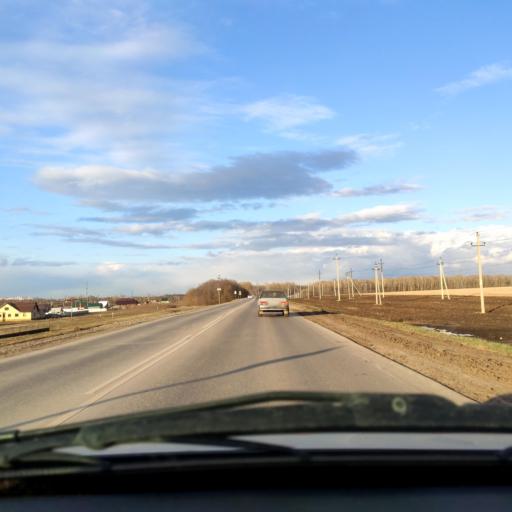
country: RU
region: Bashkortostan
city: Avdon
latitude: 54.6076
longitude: 55.8631
